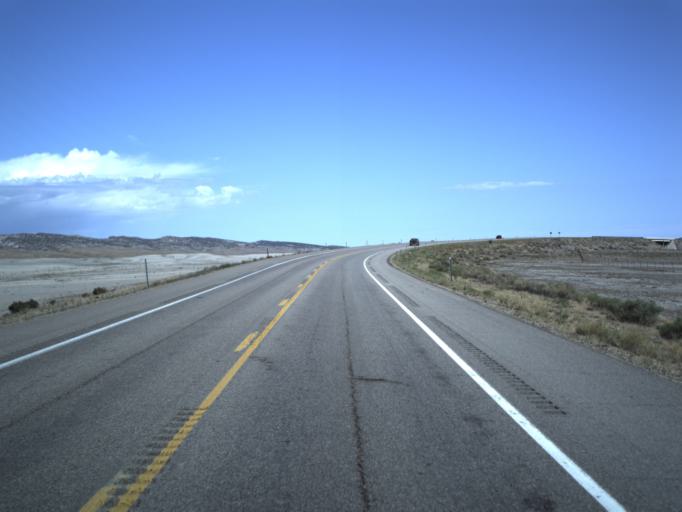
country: US
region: Utah
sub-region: Carbon County
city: East Carbon City
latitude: 39.1290
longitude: -110.3360
